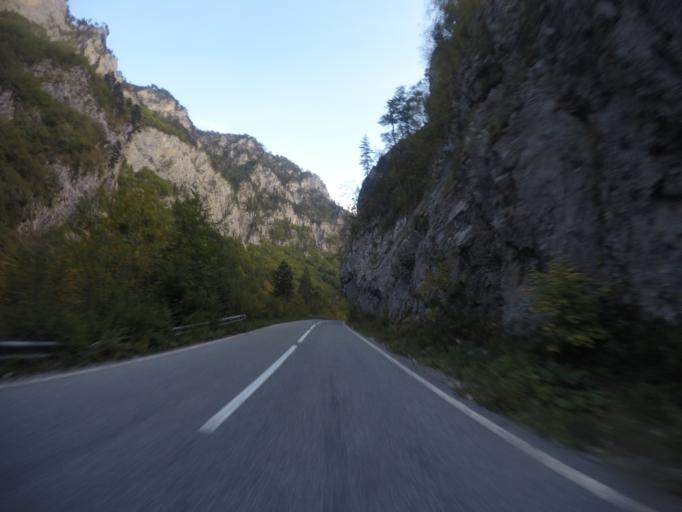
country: ME
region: Mojkovac
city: Mojkovac
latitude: 43.0717
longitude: 19.3842
